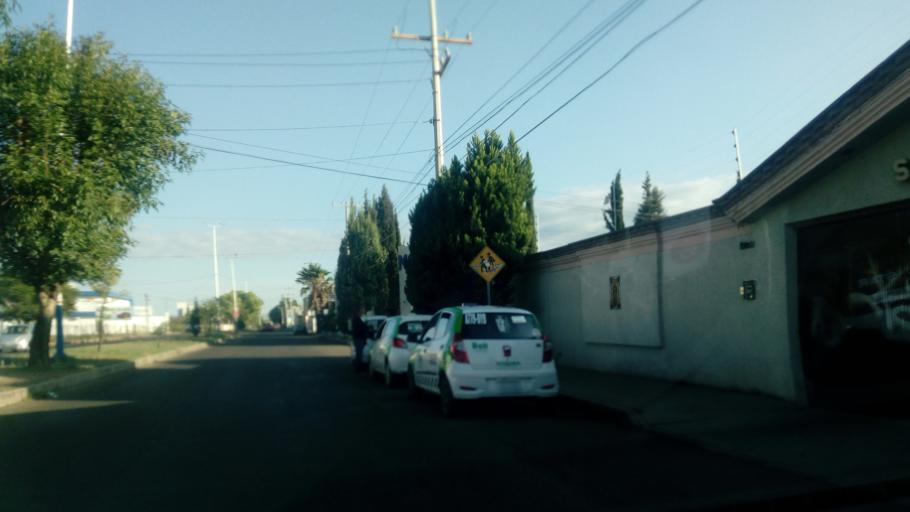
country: MX
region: Durango
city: Victoria de Durango
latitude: 24.0397
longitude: -104.6091
